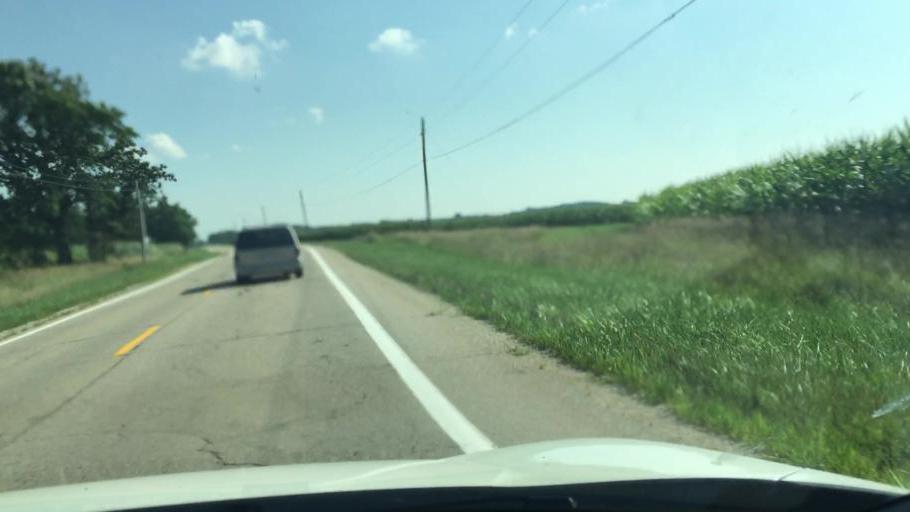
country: US
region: Ohio
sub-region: Champaign County
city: North Lewisburg
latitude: 40.1518
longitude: -83.5289
